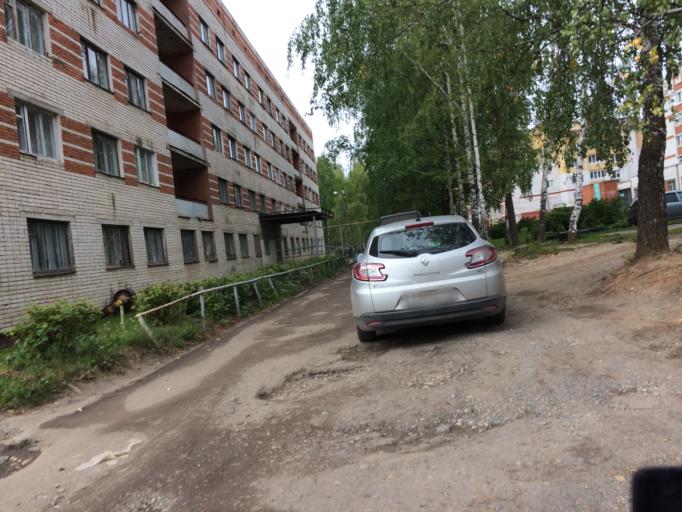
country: RU
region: Mariy-El
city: Yoshkar-Ola
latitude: 56.6512
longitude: 47.9709
